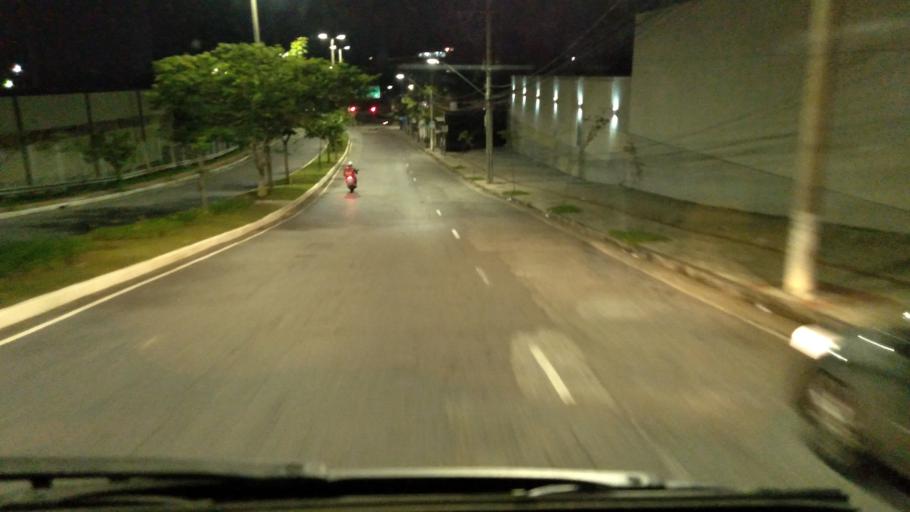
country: BR
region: Minas Gerais
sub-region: Belo Horizonte
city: Belo Horizonte
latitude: -19.8919
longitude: -43.9675
